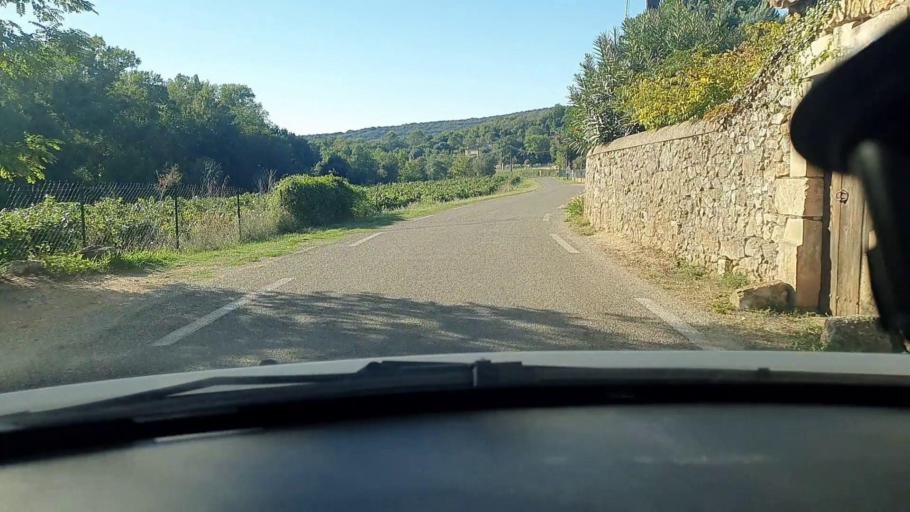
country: FR
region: Languedoc-Roussillon
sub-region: Departement du Gard
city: Goudargues
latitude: 44.2346
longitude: 4.4423
